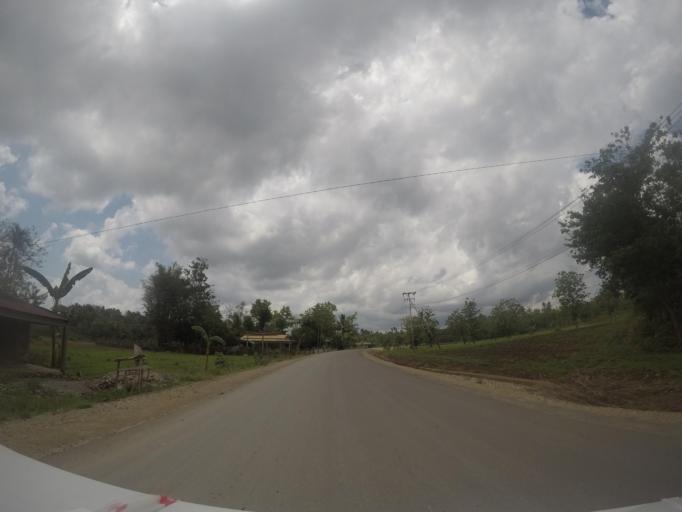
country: TL
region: Baucau
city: Baucau
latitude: -8.5366
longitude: 126.4196
